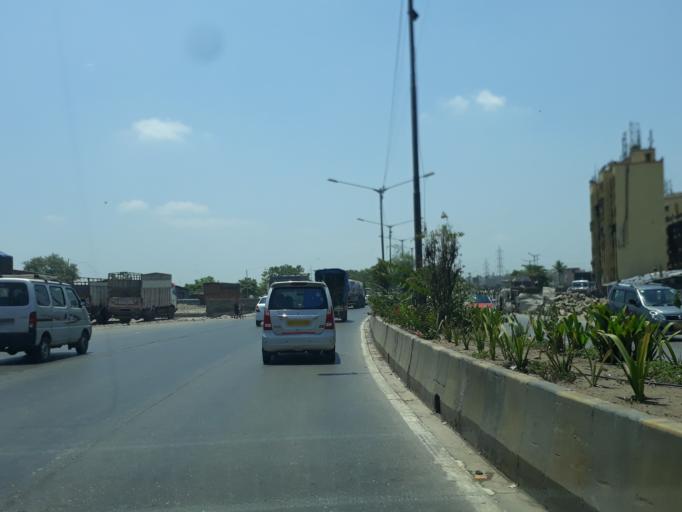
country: IN
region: Maharashtra
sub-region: Mumbai Suburban
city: Mumbai
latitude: 19.0562
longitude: 72.9318
